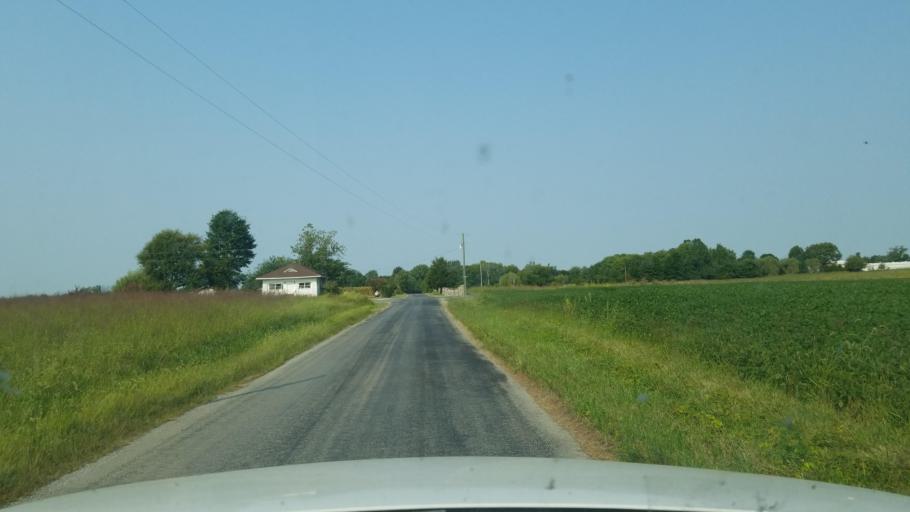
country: US
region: Illinois
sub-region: Saline County
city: Carrier Mills
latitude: 37.7906
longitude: -88.6737
